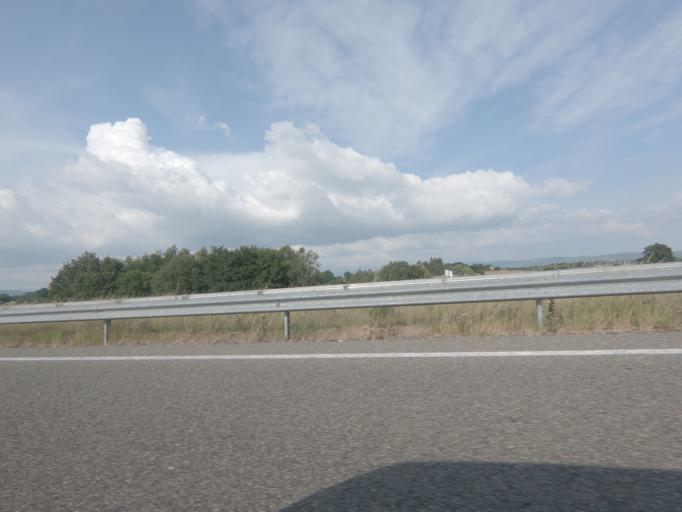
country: ES
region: Galicia
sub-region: Provincia de Ourense
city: Xinzo de Limia
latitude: 42.1215
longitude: -7.7394
